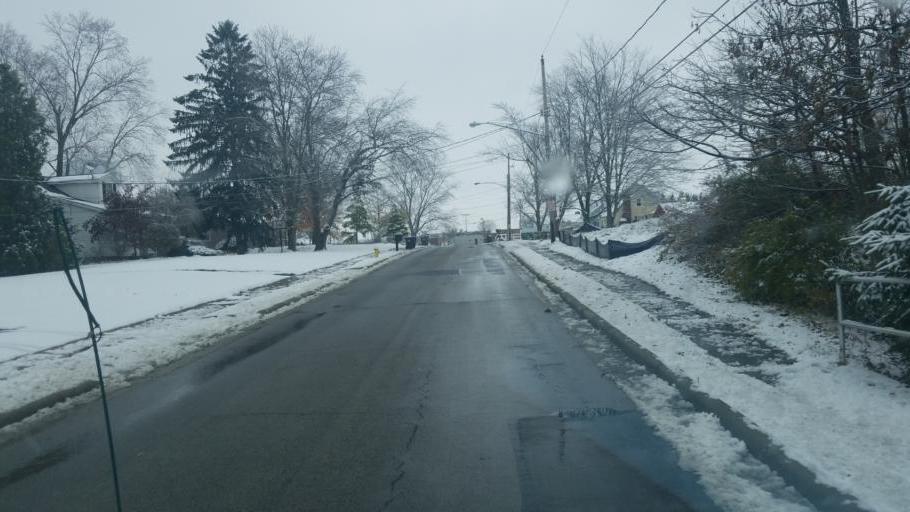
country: US
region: Ohio
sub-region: Geauga County
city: Middlefield
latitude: 41.4659
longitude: -81.0716
